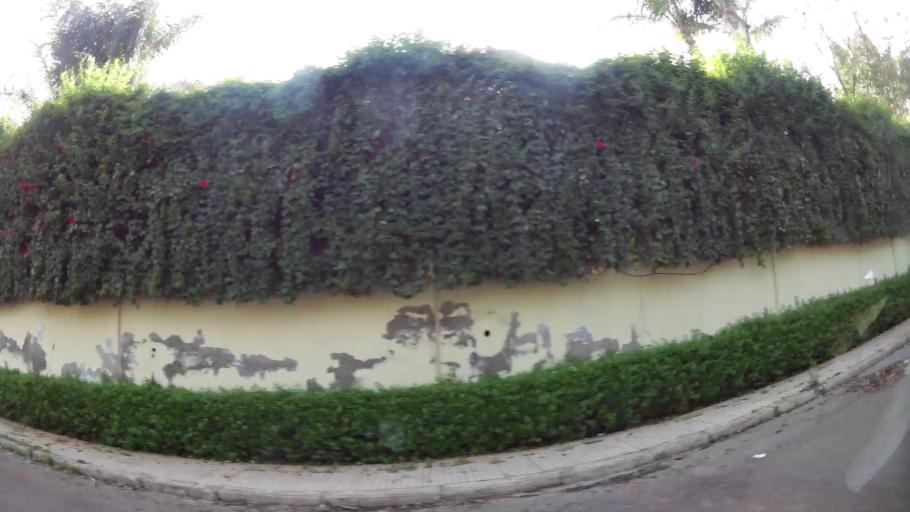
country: MA
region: Rabat-Sale-Zemmour-Zaer
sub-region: Rabat
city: Rabat
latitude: 33.9356
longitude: -6.8052
